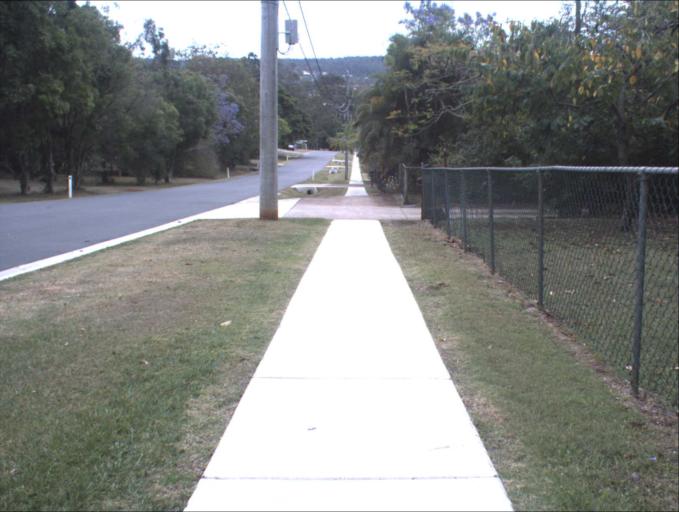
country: AU
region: Queensland
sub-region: Logan
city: Slacks Creek
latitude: -27.6623
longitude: 153.1643
